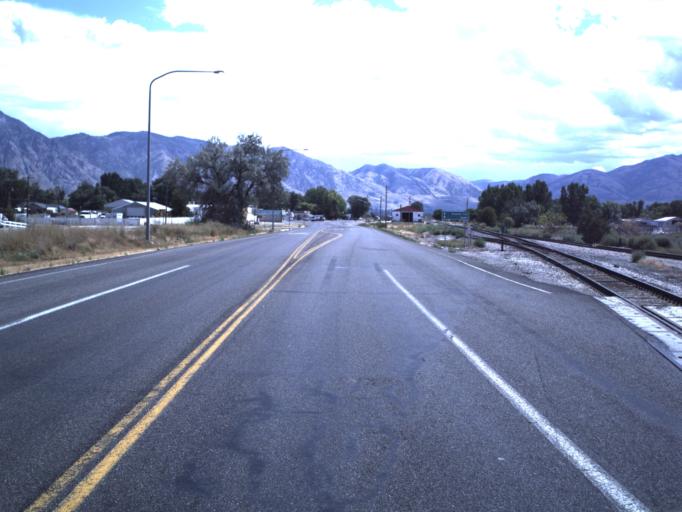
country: US
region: Utah
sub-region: Box Elder County
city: Honeyville
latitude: 41.5521
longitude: -112.1148
